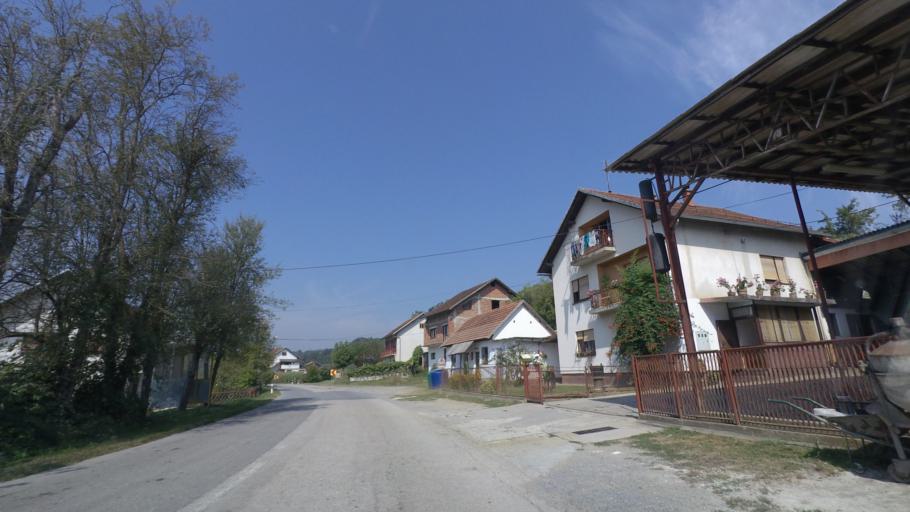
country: HR
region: Sisacko-Moslavacka
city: Dvor
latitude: 45.0819
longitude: 16.3393
